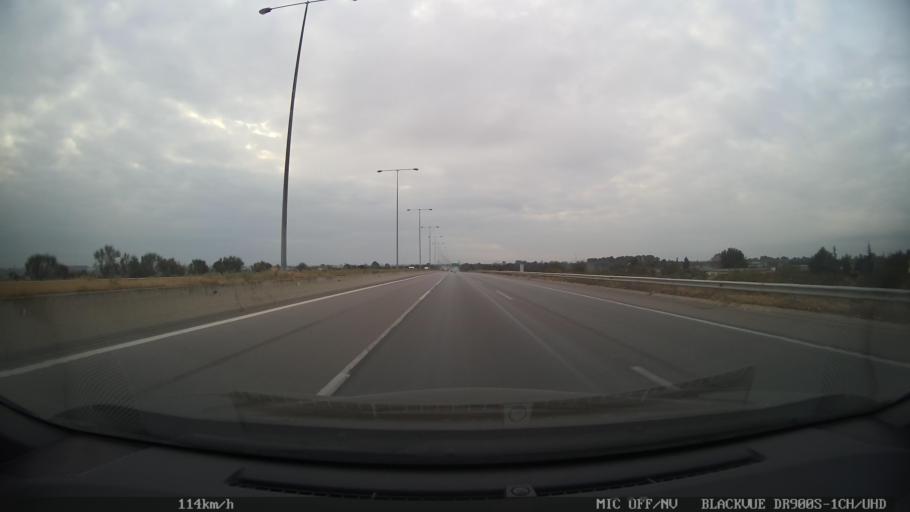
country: GR
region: Central Macedonia
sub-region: Nomos Thessalonikis
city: Nea Magnisia
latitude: 40.6668
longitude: 22.8356
